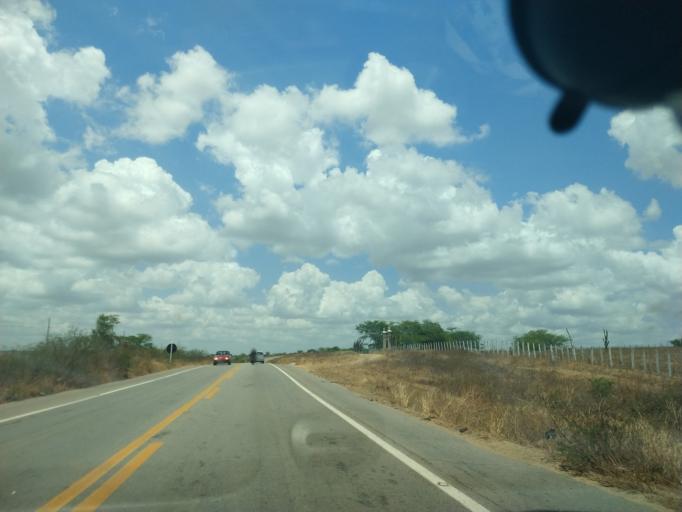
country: BR
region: Rio Grande do Norte
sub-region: Tangara
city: Tangara
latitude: -6.1852
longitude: -35.7769
